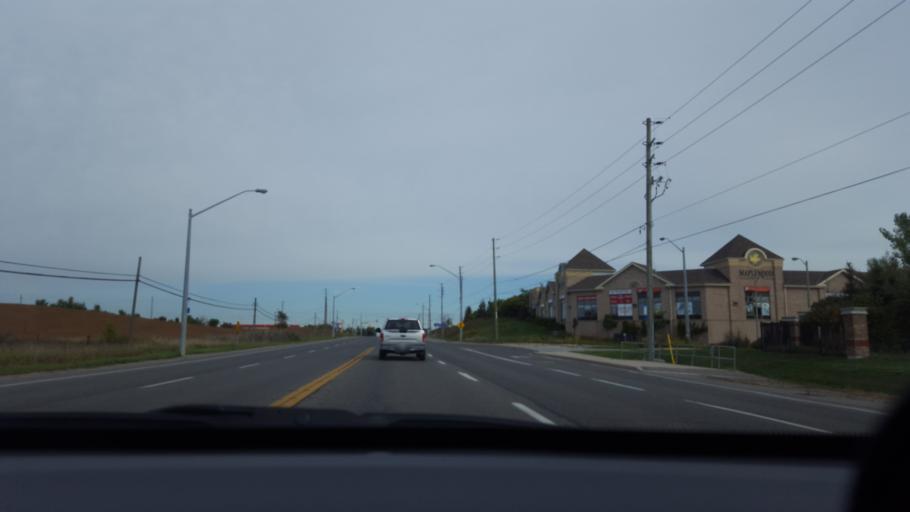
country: CA
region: Ontario
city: Vaughan
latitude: 43.8892
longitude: -79.5203
